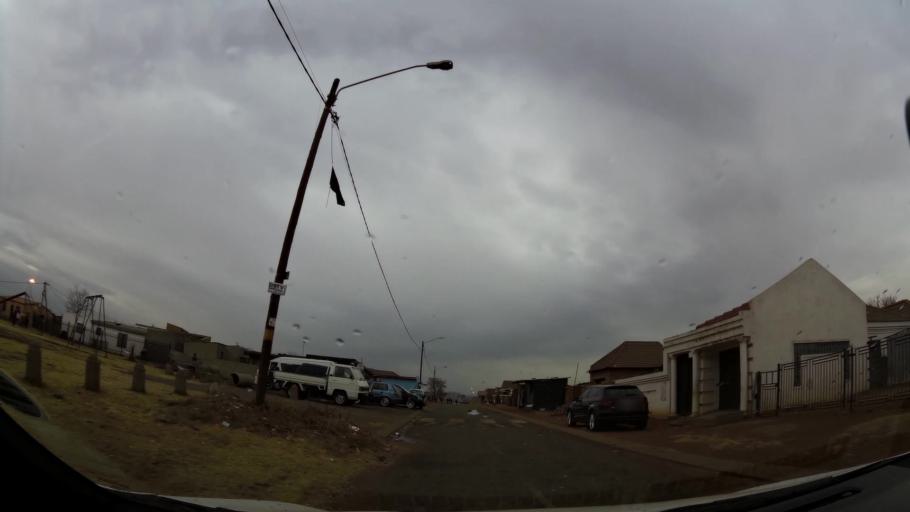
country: ZA
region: Gauteng
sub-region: Ekurhuleni Metropolitan Municipality
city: Germiston
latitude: -26.3864
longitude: 28.1762
